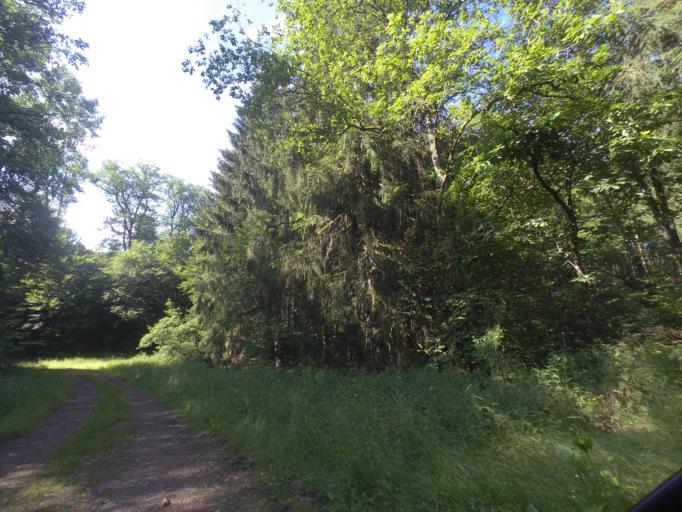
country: DE
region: Rheinland-Pfalz
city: Gonnersdorf
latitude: 50.3521
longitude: 6.5965
